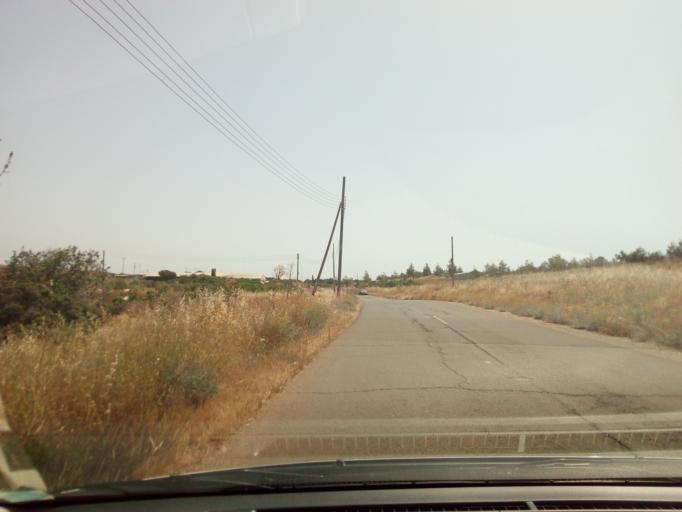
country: CY
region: Larnaka
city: Xylotymbou
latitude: 34.9862
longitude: 33.7968
